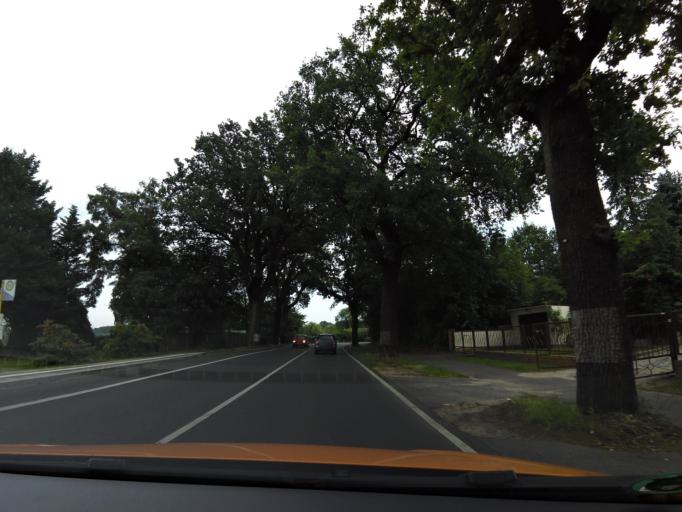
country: DE
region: Brandenburg
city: Werder
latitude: 52.3607
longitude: 12.9492
